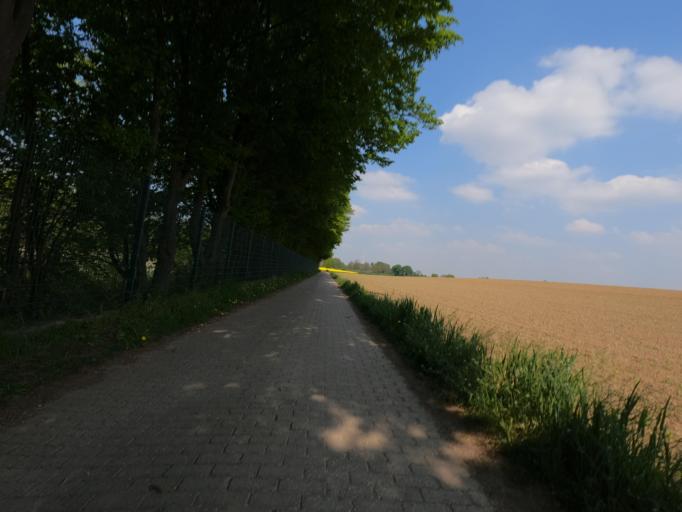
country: DE
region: North Rhine-Westphalia
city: Baesweiler
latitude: 50.9504
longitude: 6.2142
